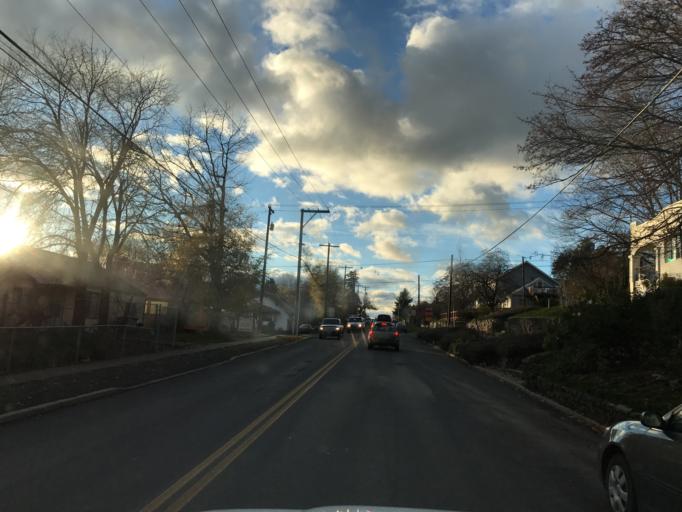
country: US
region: Idaho
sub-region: Latah County
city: Moscow
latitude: 46.7345
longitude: -117.0112
